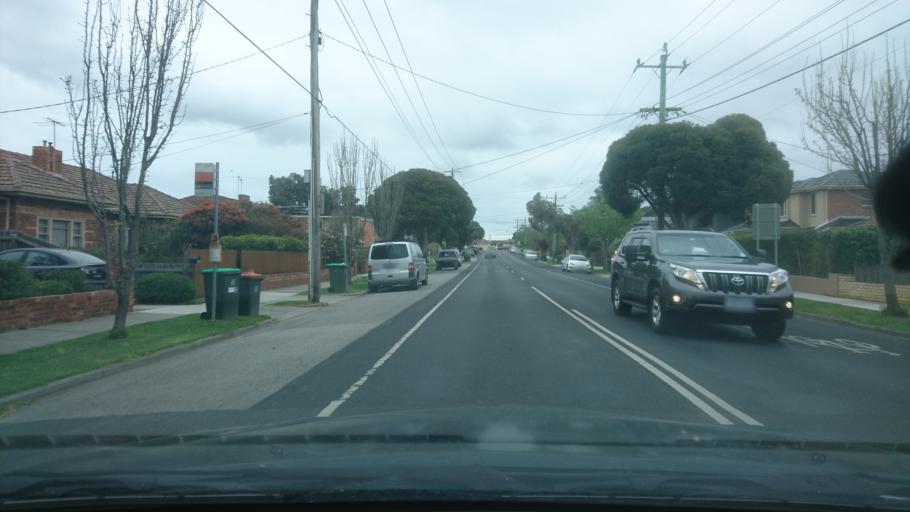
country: AU
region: Victoria
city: Murrumbeena
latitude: -37.8974
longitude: 145.0675
